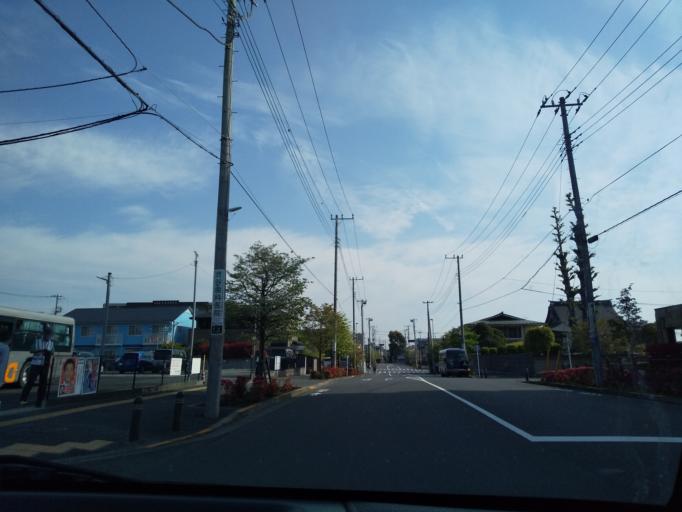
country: JP
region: Tokyo
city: Hino
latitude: 35.6820
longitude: 139.3941
